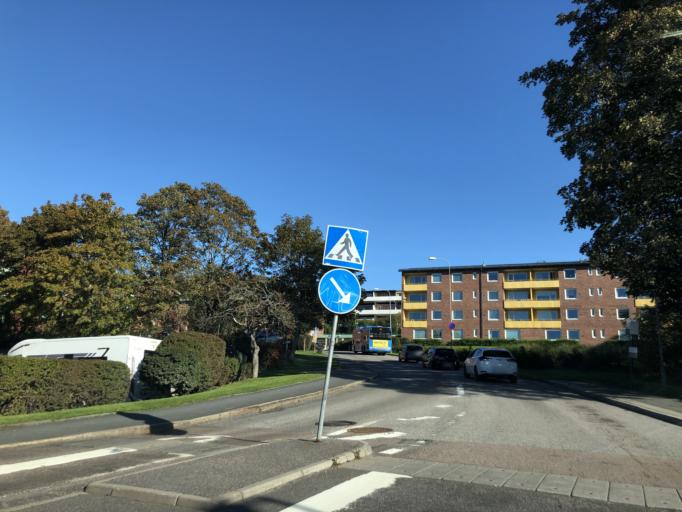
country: SE
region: Vaestra Goetaland
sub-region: Molndal
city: Moelndal
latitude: 57.6799
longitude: 12.0146
